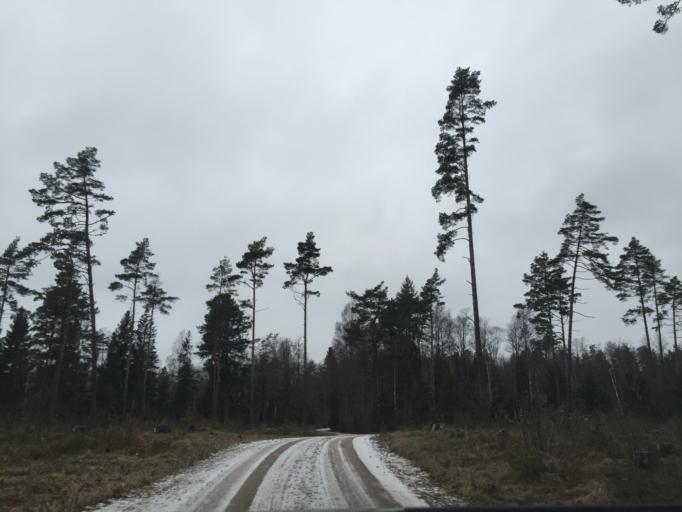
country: EE
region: Saare
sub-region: Kuressaare linn
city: Kuressaare
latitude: 58.3944
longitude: 22.2566
